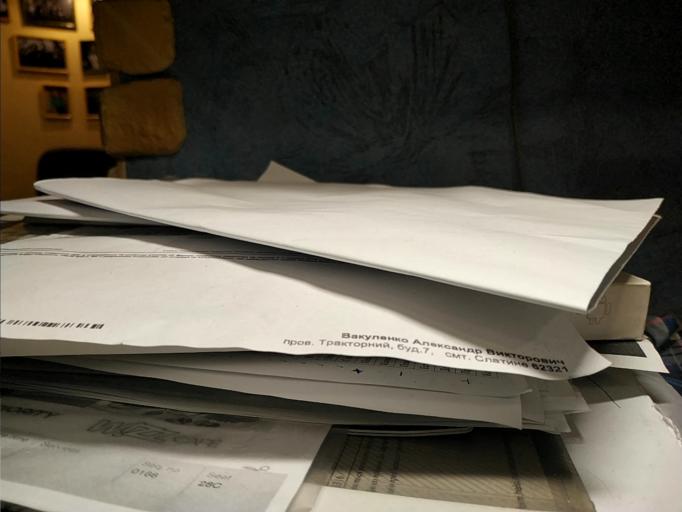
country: RU
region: Tverskaya
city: Zubtsov
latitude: 56.0901
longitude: 34.7460
